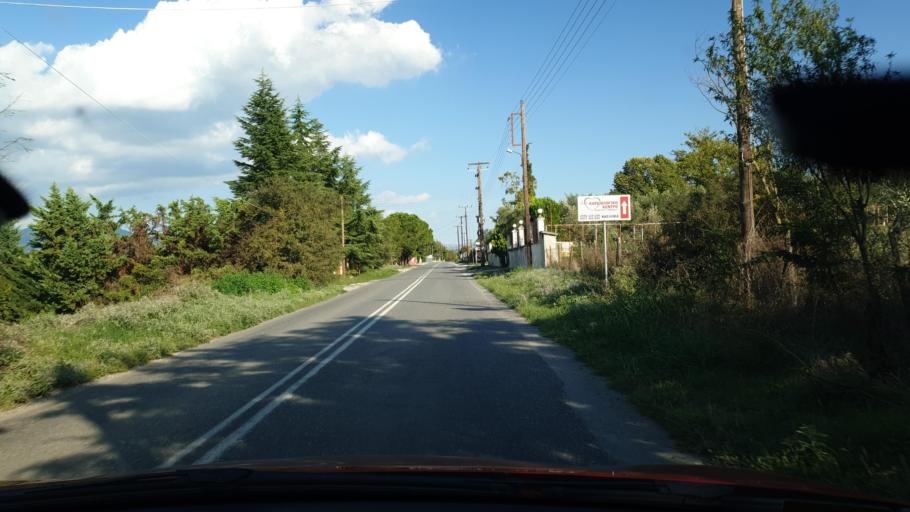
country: GR
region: Central Macedonia
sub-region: Nomos Thessalonikis
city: Souroti
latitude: 40.4795
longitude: 23.0720
